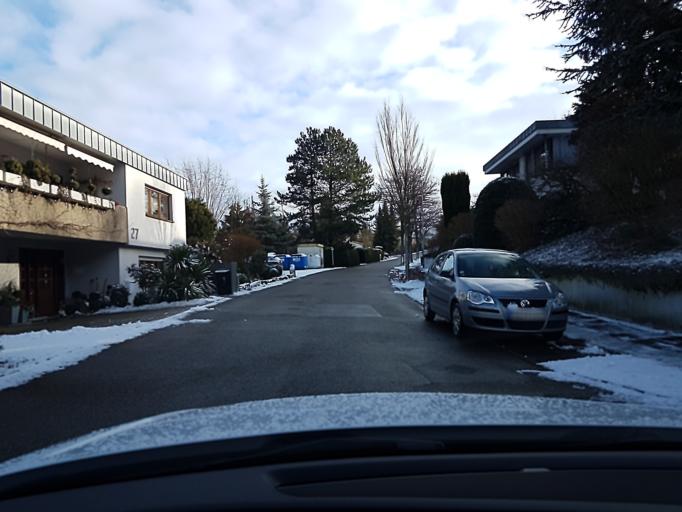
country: DE
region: Baden-Wuerttemberg
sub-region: Regierungsbezirk Stuttgart
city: Weinsberg
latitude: 49.1445
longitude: 9.2853
